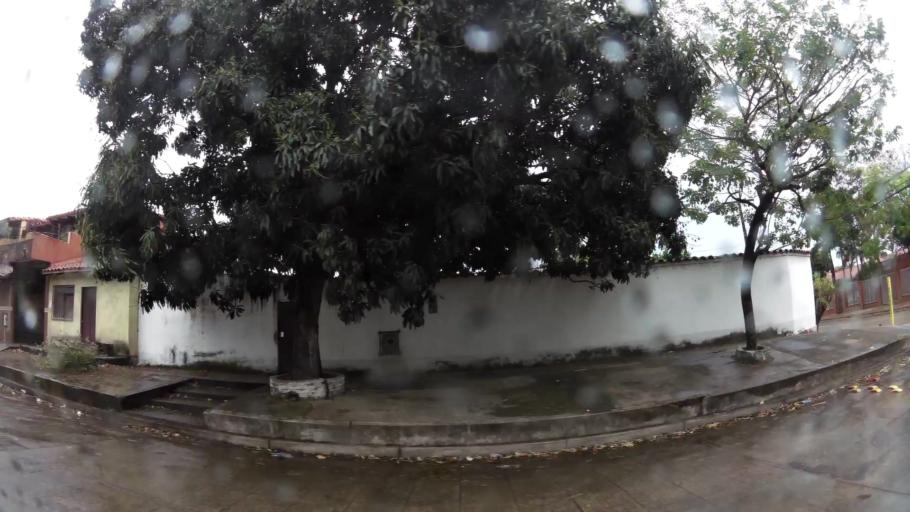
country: BO
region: Santa Cruz
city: Santa Cruz de la Sierra
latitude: -17.8007
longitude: -63.1591
